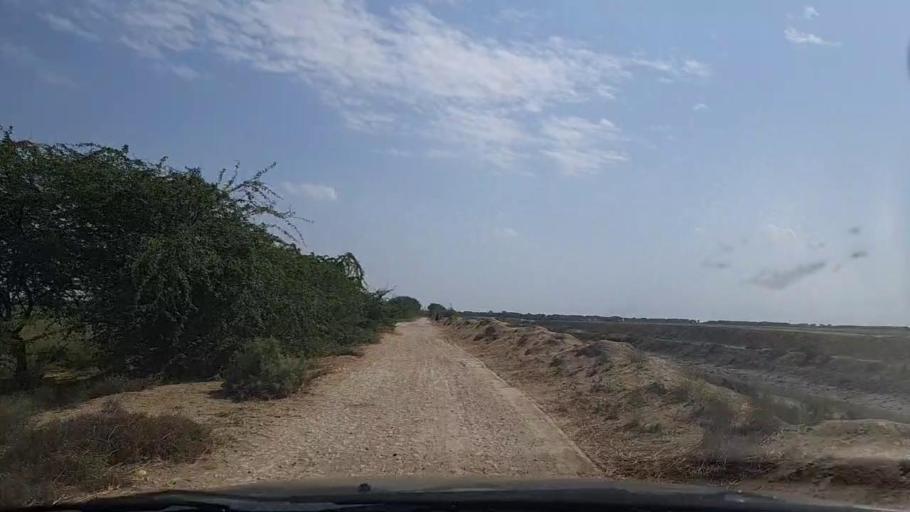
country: PK
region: Sindh
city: Mirpur Batoro
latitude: 24.5726
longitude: 68.1970
